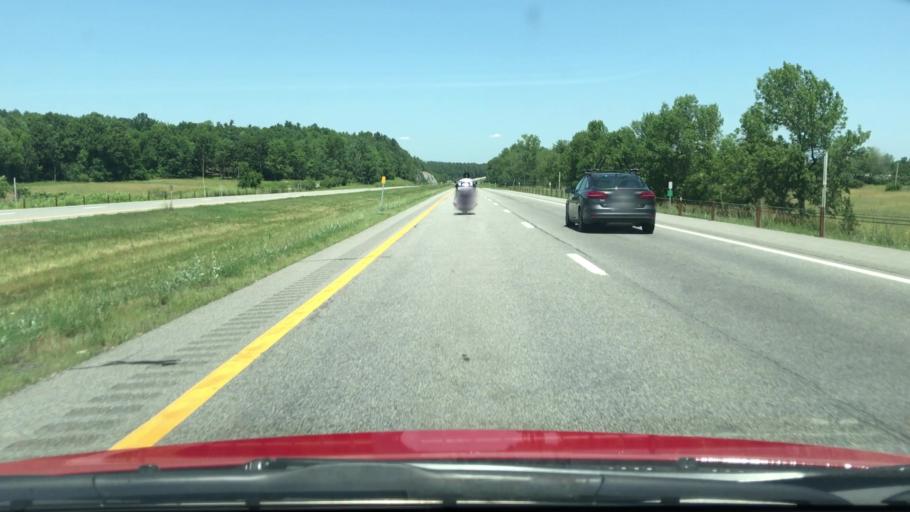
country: US
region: New York
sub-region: Essex County
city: Keeseville
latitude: 44.4678
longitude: -73.4859
